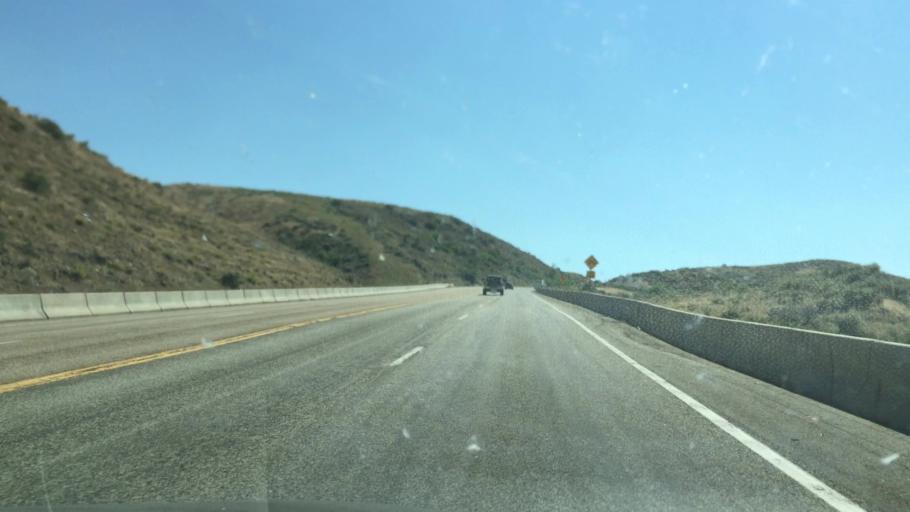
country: US
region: Idaho
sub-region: Ada County
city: Eagle
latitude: 43.8406
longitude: -116.2369
